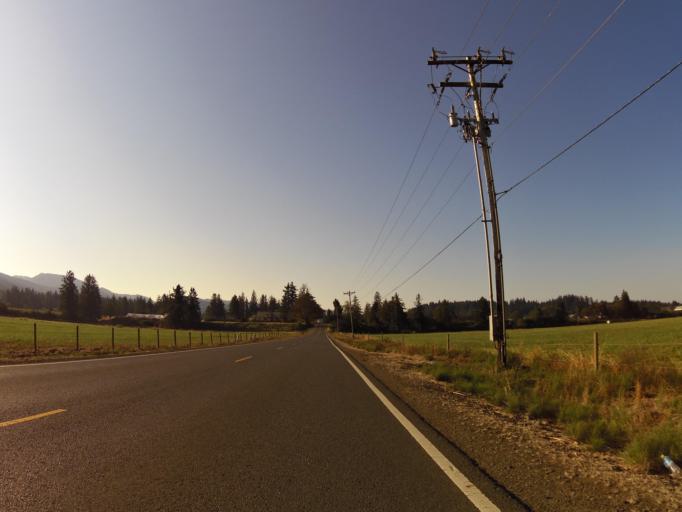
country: US
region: Oregon
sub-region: Tillamook County
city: Tillamook
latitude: 45.4342
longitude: -123.7779
